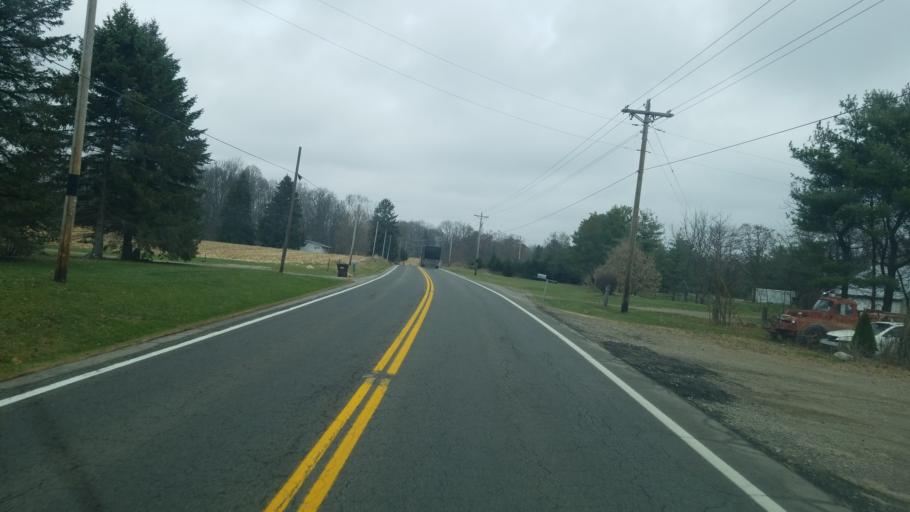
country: US
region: Ohio
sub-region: Huron County
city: Greenwich
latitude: 41.0876
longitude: -82.4875
